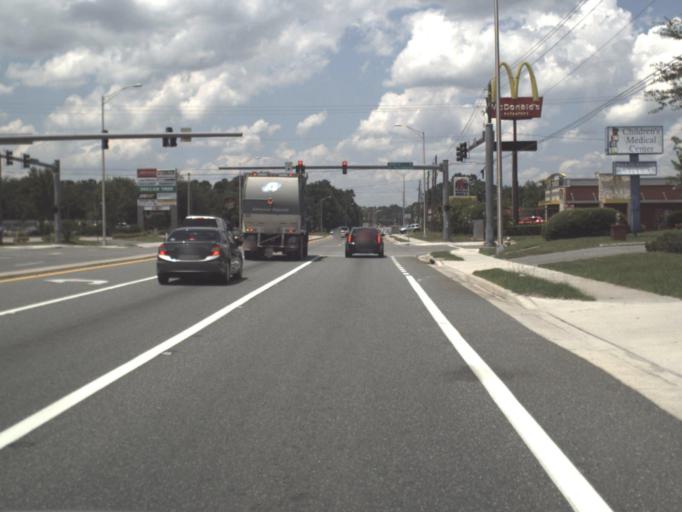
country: US
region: Florida
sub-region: Baker County
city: Macclenny
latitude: 30.2646
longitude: -82.1227
